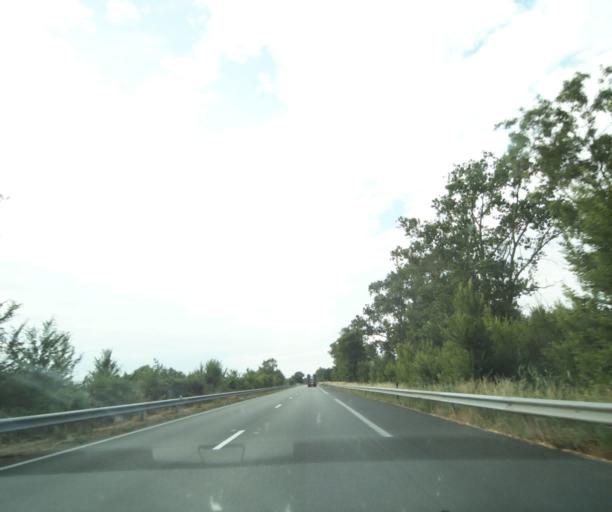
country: FR
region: Poitou-Charentes
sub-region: Departement de la Charente-Maritime
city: Chatelaillon-Plage
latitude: 46.0706
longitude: -1.0683
